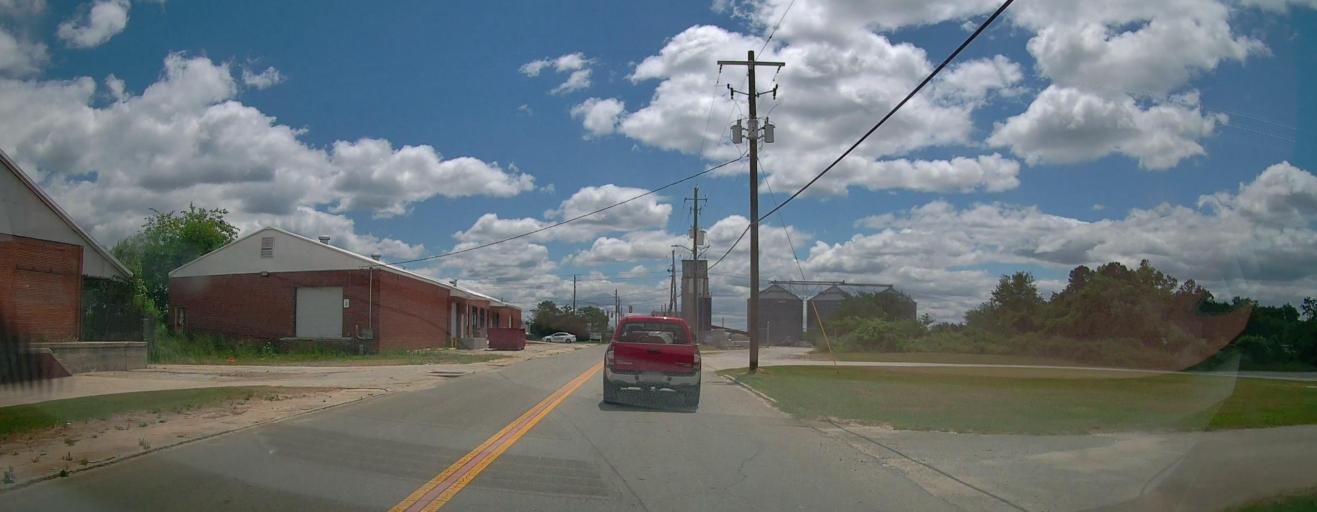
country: US
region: Georgia
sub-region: Bibb County
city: Macon
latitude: 32.8315
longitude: -83.6237
